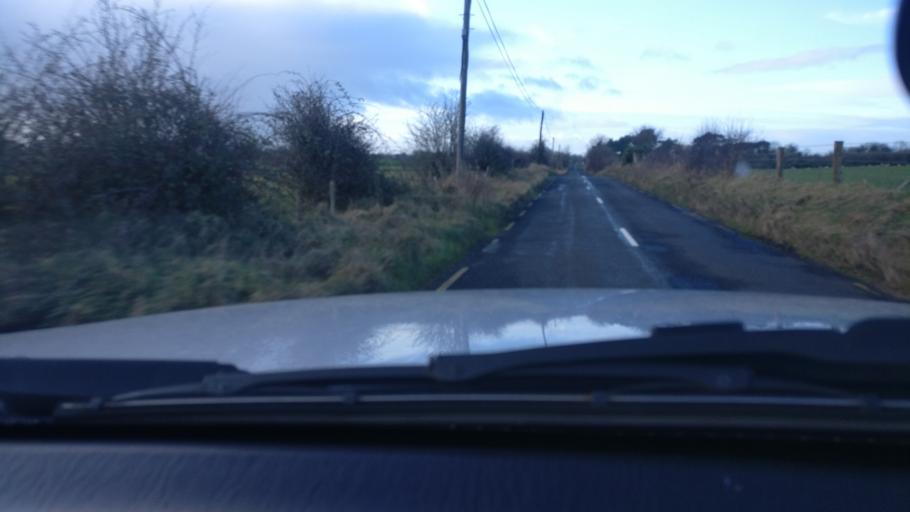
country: IE
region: Connaught
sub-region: County Galway
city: Ballinasloe
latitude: 53.2295
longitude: -8.3261
